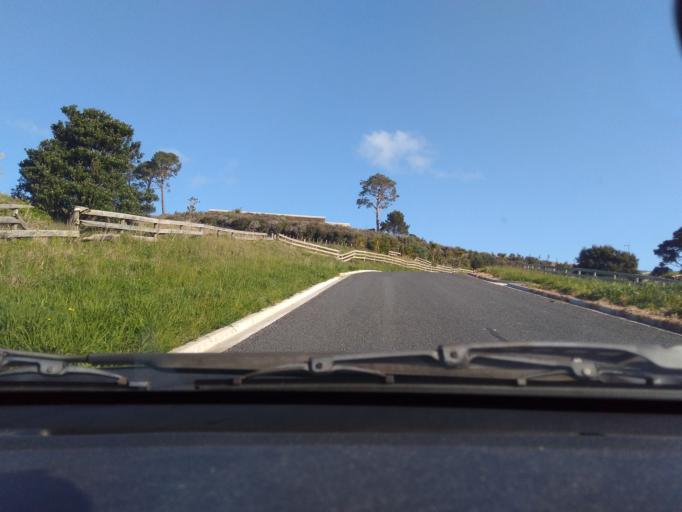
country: NZ
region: Auckland
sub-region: Auckland
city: Warkworth
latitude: -36.4438
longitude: 174.7515
